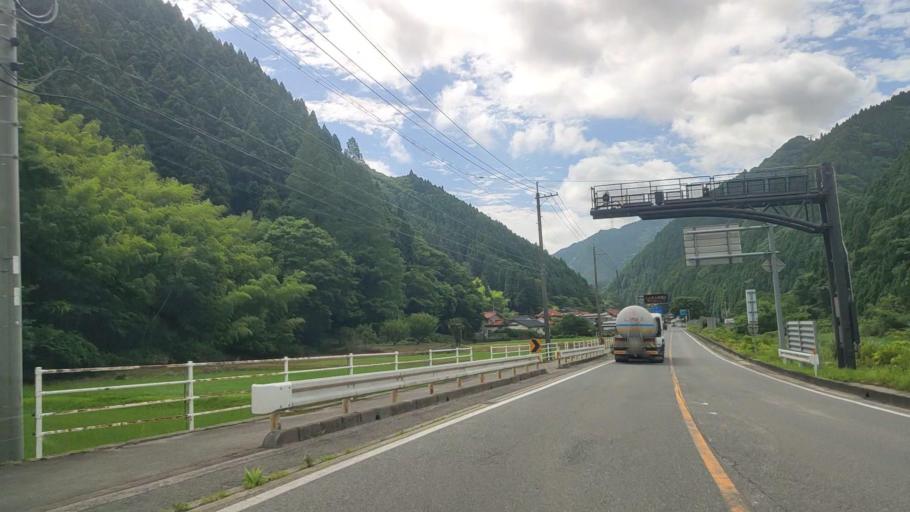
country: JP
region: Tottori
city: Yonago
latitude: 35.2308
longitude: 133.4426
